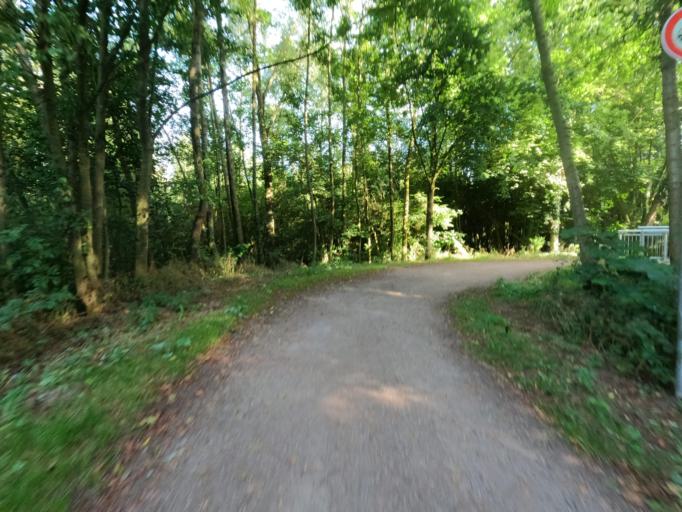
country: DE
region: North Rhine-Westphalia
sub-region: Regierungsbezirk Dusseldorf
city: Bruggen
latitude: 51.2364
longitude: 6.1578
